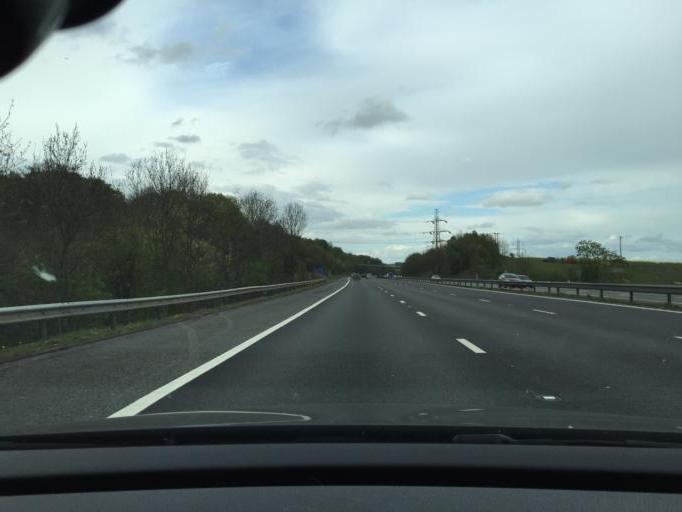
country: GB
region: England
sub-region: West Berkshire
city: Basildon
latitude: 51.4597
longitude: -1.1220
